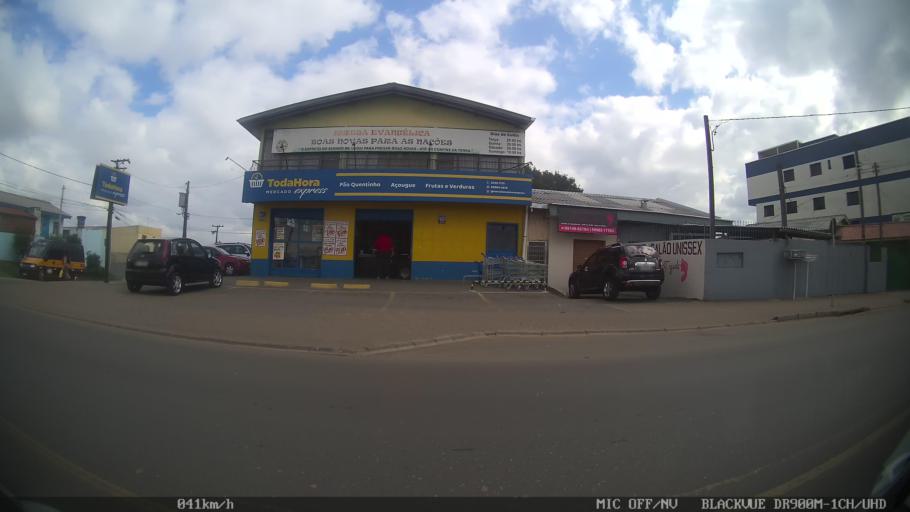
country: BR
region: Parana
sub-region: Colombo
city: Colombo
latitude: -25.3638
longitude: -49.2018
